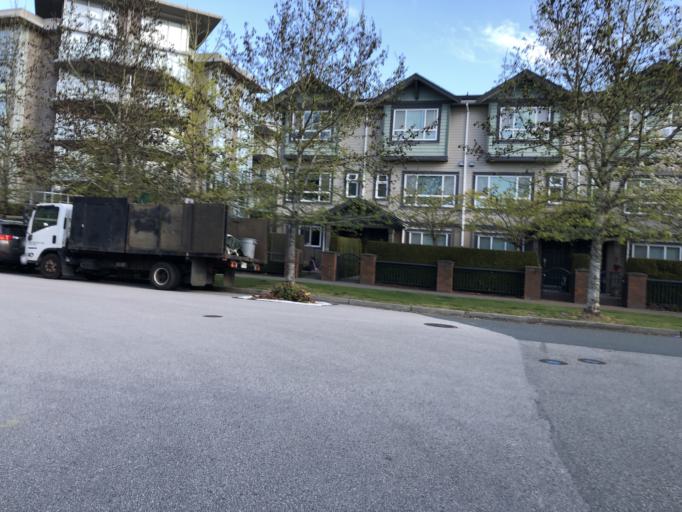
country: CA
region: British Columbia
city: Richmond
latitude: 49.1670
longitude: -123.1195
